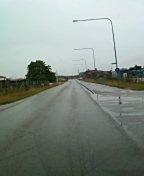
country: SE
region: Vaestmanland
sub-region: Kopings Kommun
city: Koping
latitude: 59.5030
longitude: 16.0001
